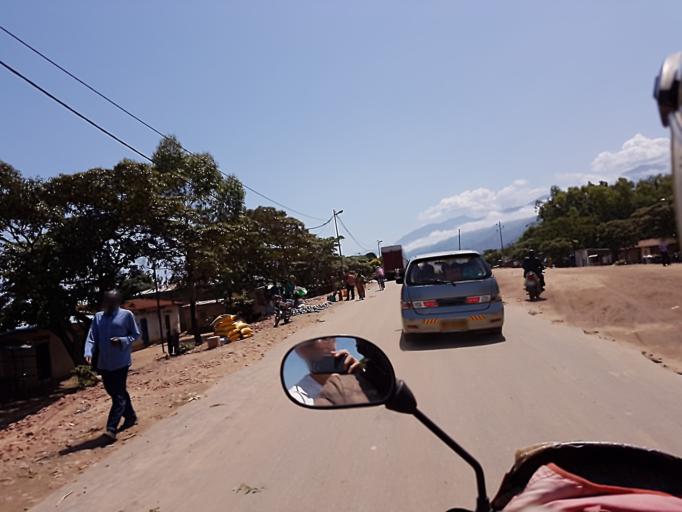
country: CD
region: South Kivu
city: Uvira
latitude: -3.3534
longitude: 29.1550
